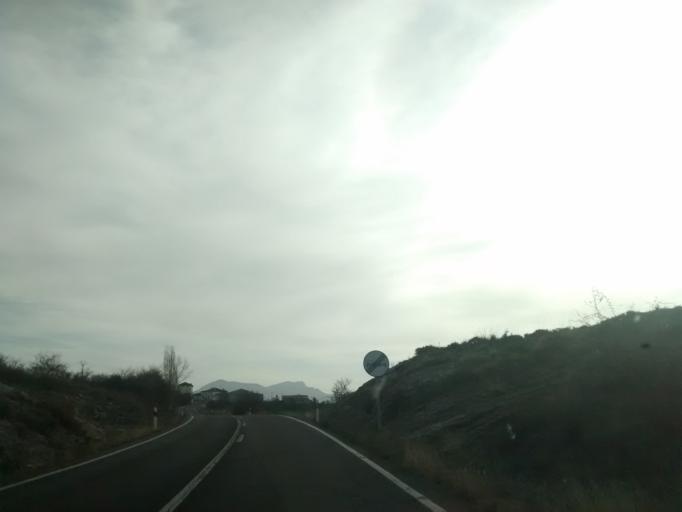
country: ES
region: Aragon
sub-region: Provincia de Zaragoza
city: Mianos
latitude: 42.6017
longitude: -0.8640
